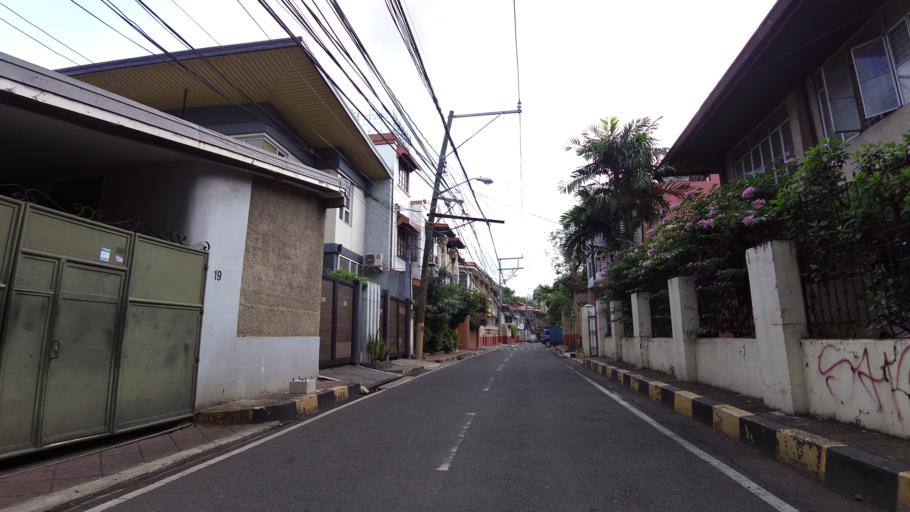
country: PH
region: Calabarzon
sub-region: Province of Rizal
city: Pateros
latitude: 14.5608
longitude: 121.0748
